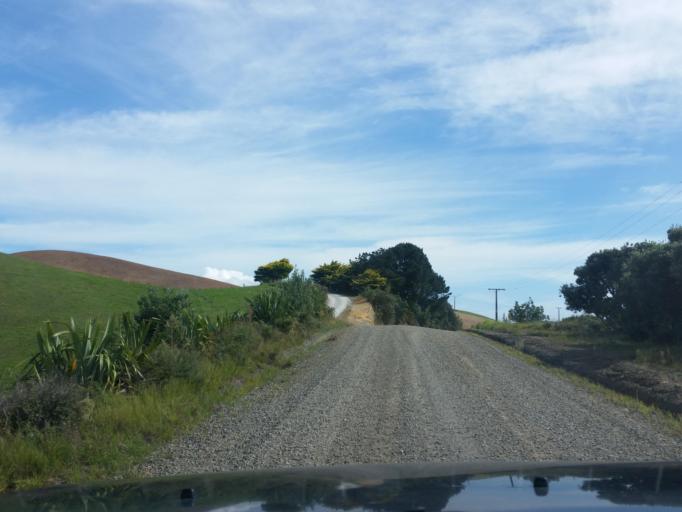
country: NZ
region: Northland
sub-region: Kaipara District
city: Dargaville
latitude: -35.9263
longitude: 173.7390
